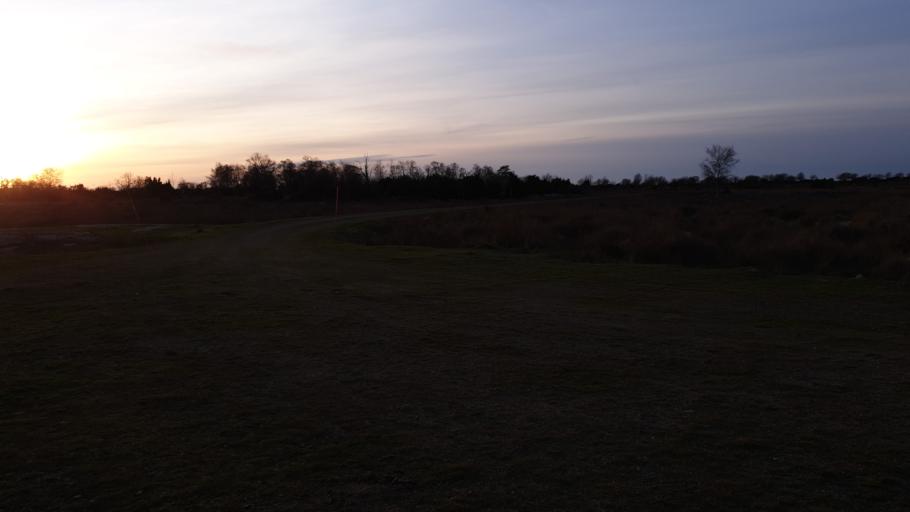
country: SE
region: Blekinge
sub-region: Karlskrona Kommun
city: Jaemjoe
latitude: 56.0782
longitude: 15.8499
